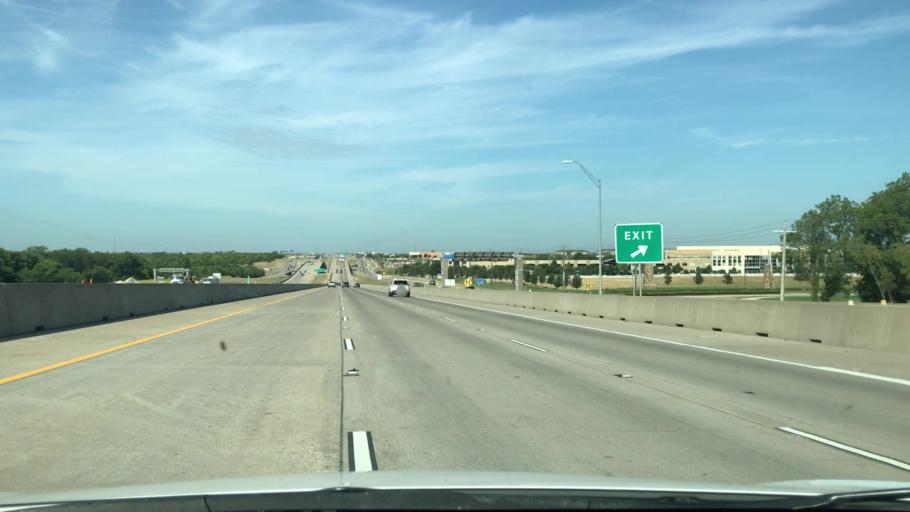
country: US
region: Texas
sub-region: Collin County
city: Allen
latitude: 33.1330
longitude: -96.7107
